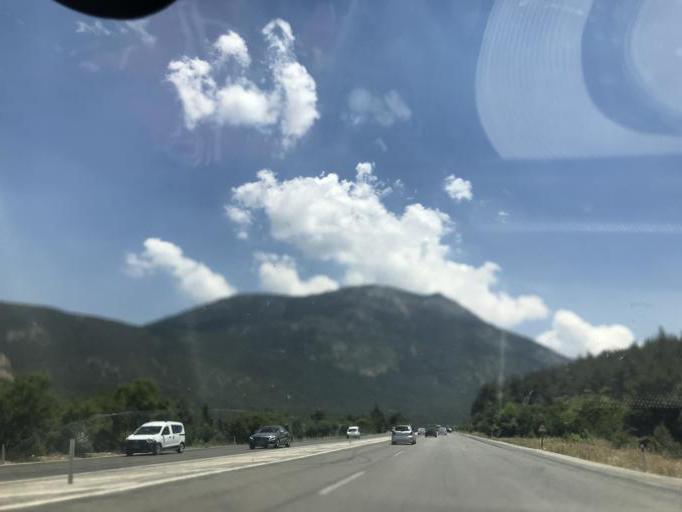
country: TR
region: Denizli
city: Honaz
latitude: 37.7269
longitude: 29.2010
